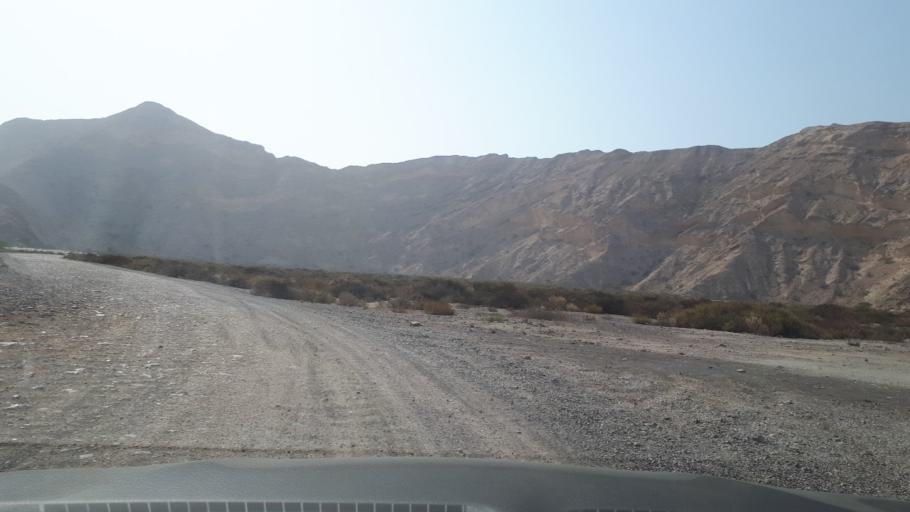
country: OM
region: Muhafazat Masqat
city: Muscat
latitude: 23.5392
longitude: 58.6618
